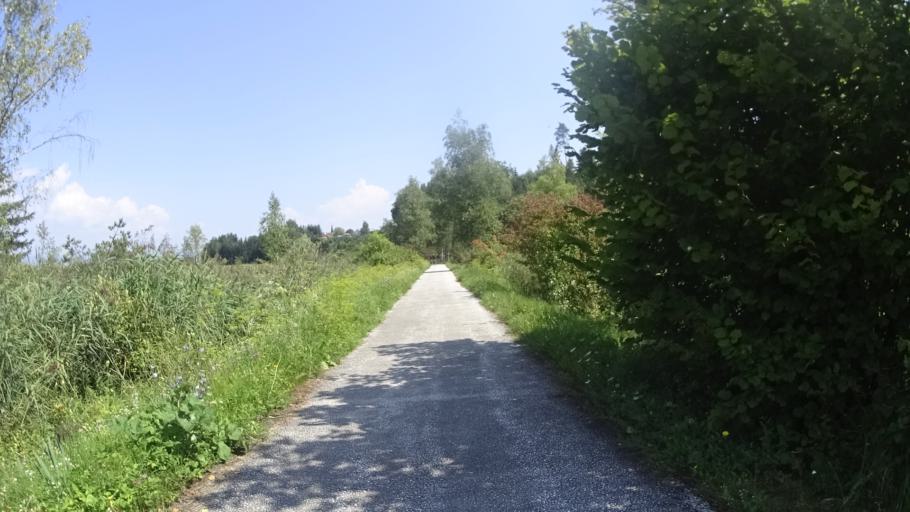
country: AT
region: Carinthia
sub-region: Politischer Bezirk Volkermarkt
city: Eberndorf
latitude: 46.5670
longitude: 14.6301
